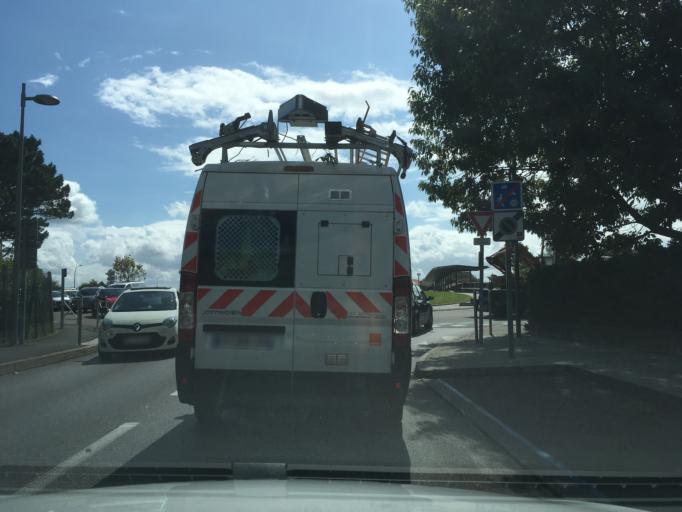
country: FR
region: Aquitaine
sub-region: Departement des Pyrenees-Atlantiques
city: Anglet
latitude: 43.4951
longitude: -1.5284
